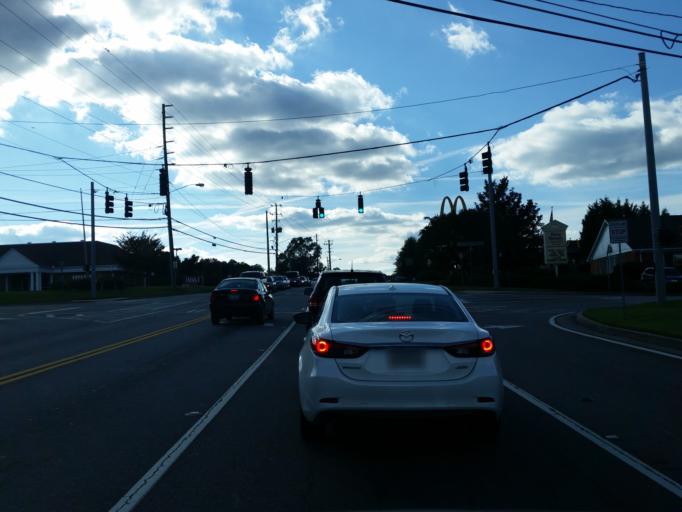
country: US
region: Georgia
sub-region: Cobb County
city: Marietta
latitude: 33.9520
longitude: -84.5742
